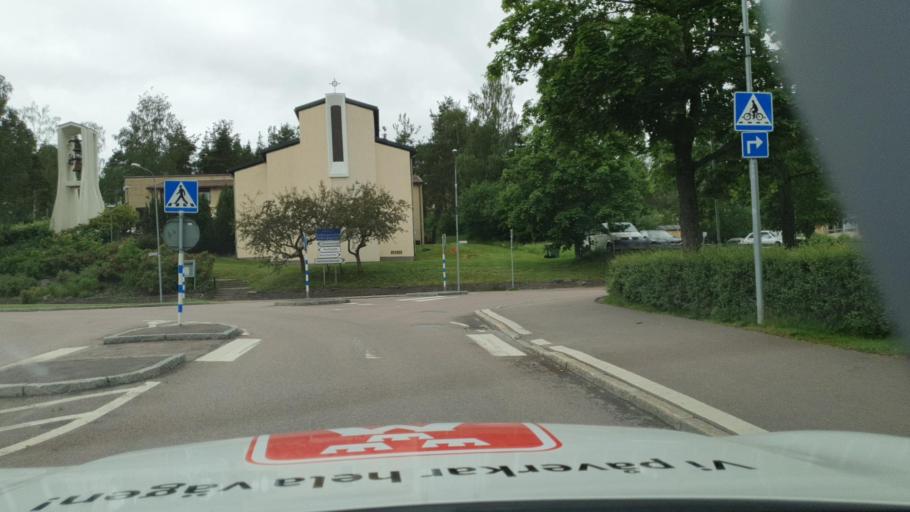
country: SE
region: Vaermland
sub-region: Grums Kommun
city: Grums
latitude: 59.3507
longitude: 13.1106
